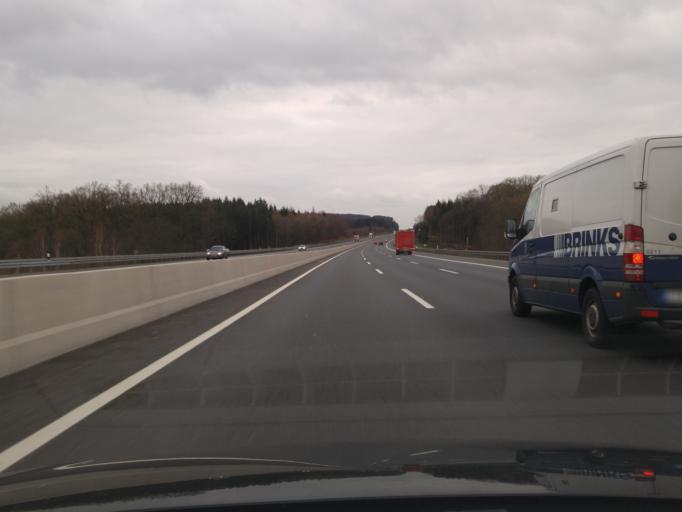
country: DE
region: Lower Saxony
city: Haverlah
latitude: 52.0531
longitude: 10.1890
